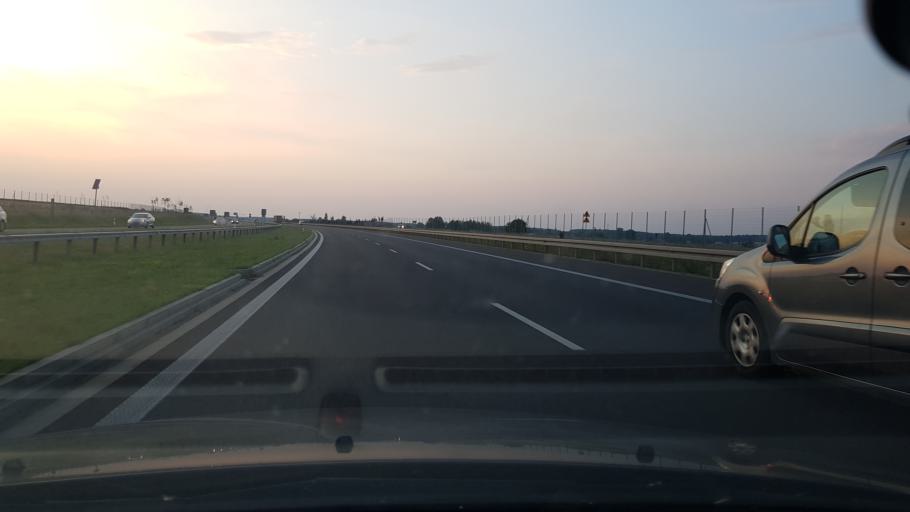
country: PL
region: Masovian Voivodeship
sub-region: Powiat mlawski
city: Wieczfnia Koscielna
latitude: 53.2170
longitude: 20.4280
